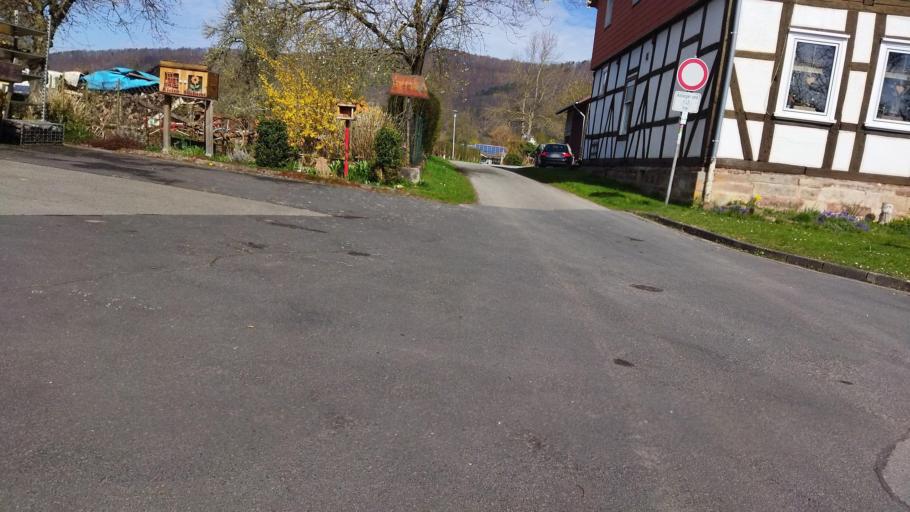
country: DE
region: Lower Saxony
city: Bodenfelde
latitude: 51.5905
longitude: 9.5918
